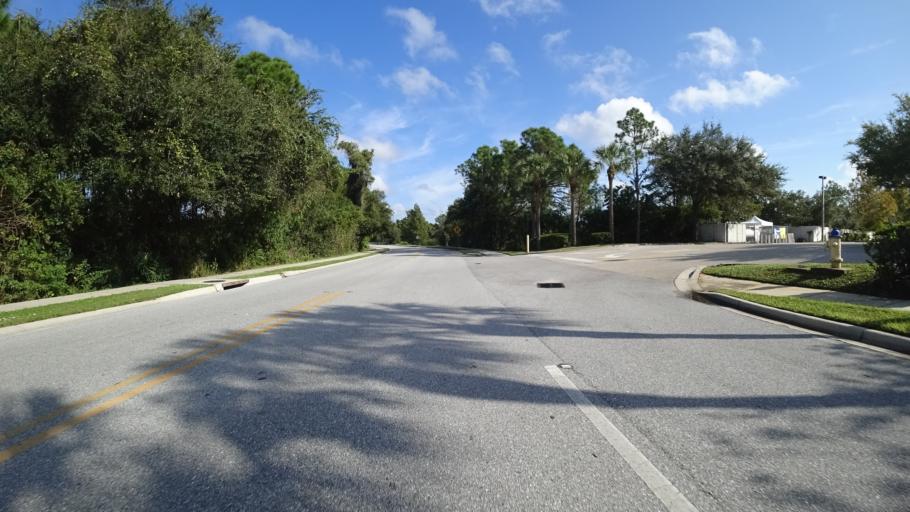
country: US
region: Florida
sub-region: Sarasota County
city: The Meadows
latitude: 27.3948
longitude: -82.4527
